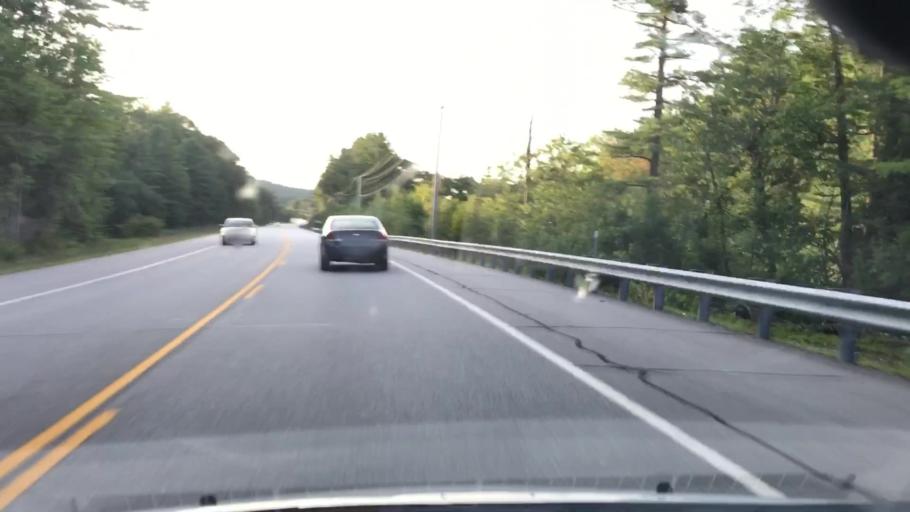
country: US
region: New Hampshire
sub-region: Grafton County
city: Rumney
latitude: 43.8076
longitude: -71.8616
